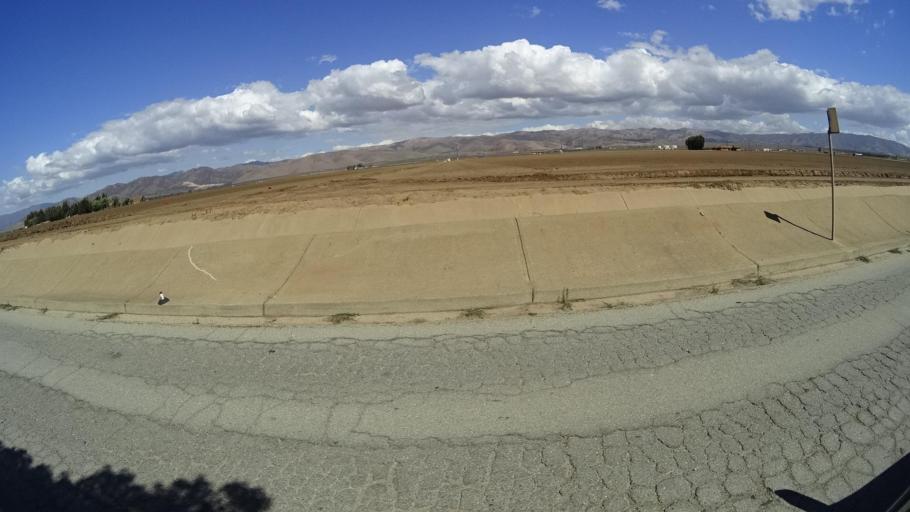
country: US
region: California
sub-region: Monterey County
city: Gonzales
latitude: 36.5219
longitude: -121.4418
